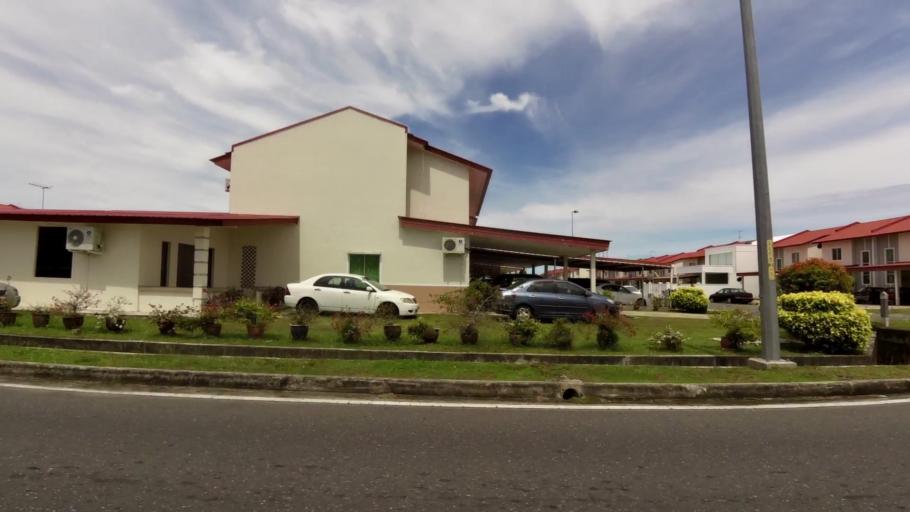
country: BN
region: Belait
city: Kuala Belait
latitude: 4.5883
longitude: 114.2704
